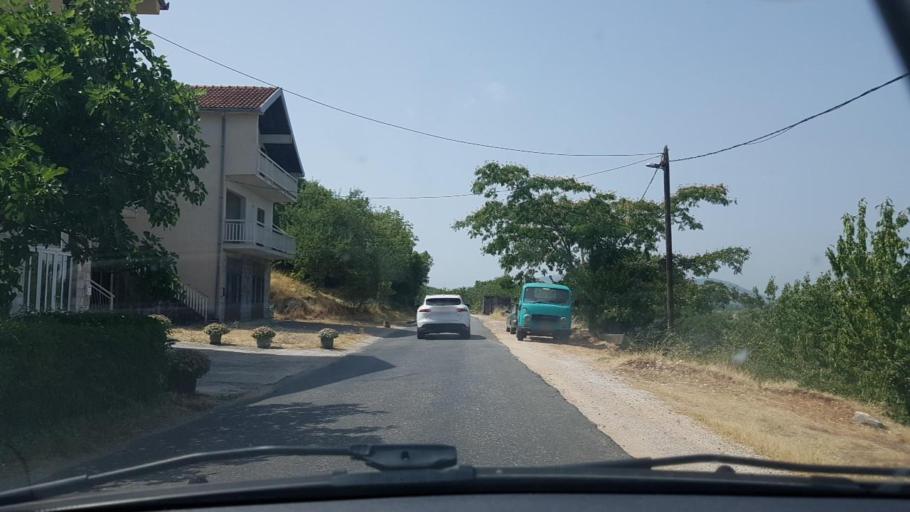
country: BA
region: Federation of Bosnia and Herzegovina
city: Tasovcici
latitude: 43.0350
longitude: 17.7254
